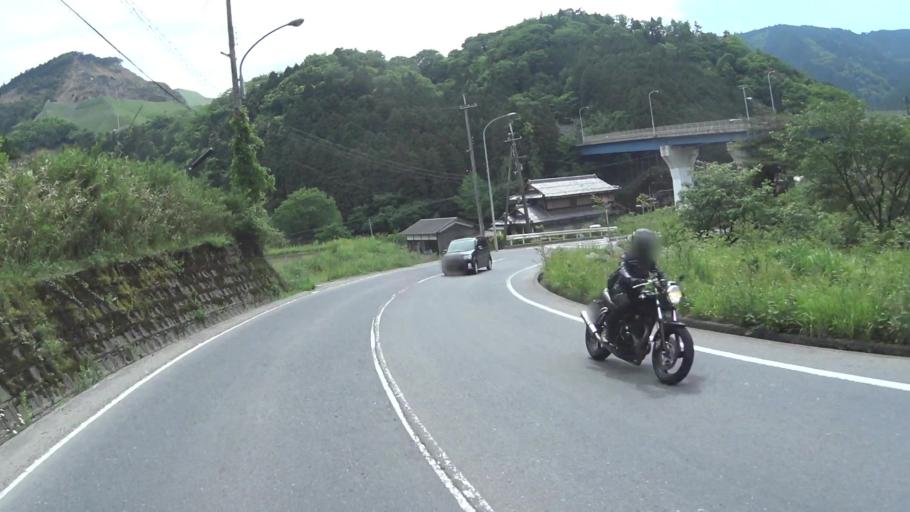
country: JP
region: Shiga Prefecture
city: Kitahama
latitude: 35.1664
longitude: 135.8612
